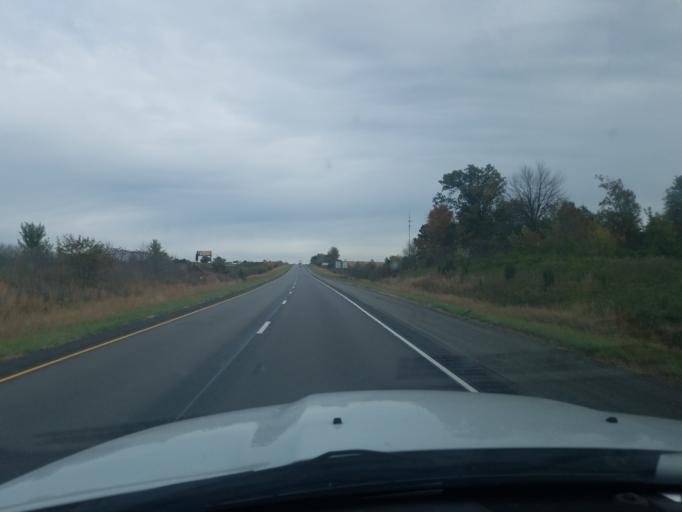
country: US
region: Indiana
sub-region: Spencer County
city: Dale
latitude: 38.1966
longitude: -86.9384
